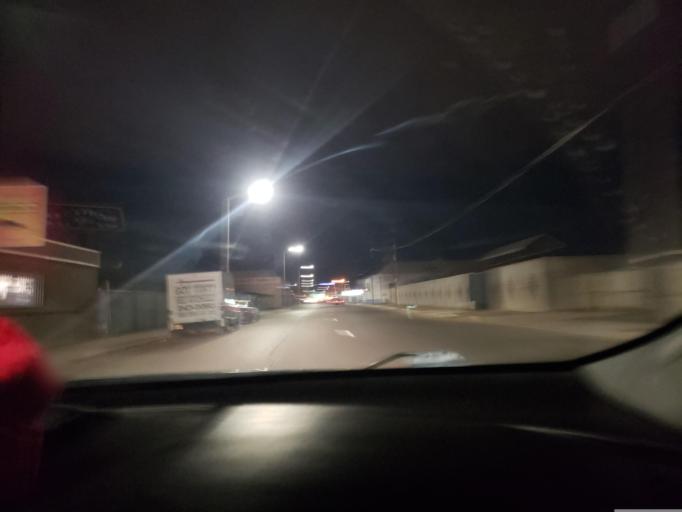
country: US
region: New Mexico
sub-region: Bernalillo County
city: Albuquerque
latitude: 35.0997
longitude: -106.6463
